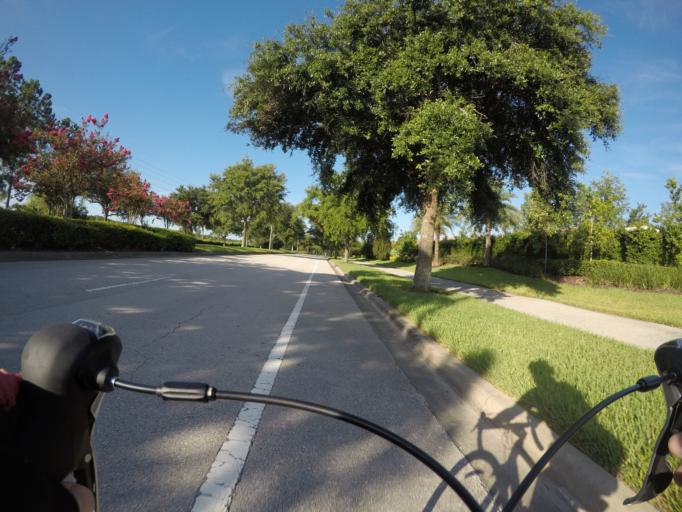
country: US
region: Florida
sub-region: Orange County
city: Meadow Woods
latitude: 28.3979
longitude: -81.2513
